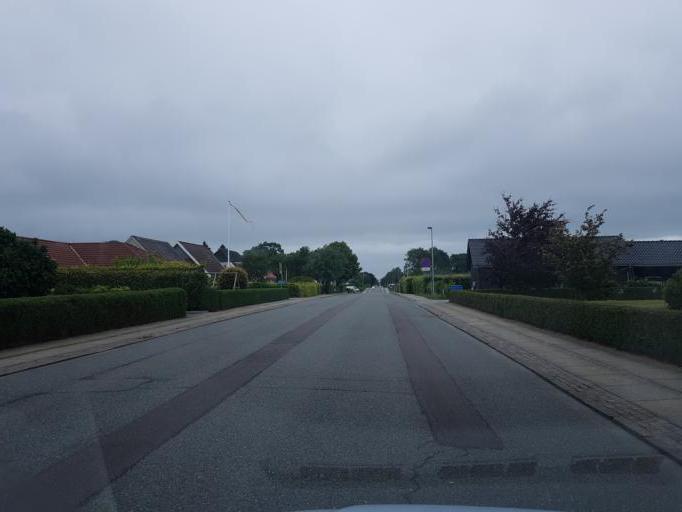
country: DK
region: South Denmark
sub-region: Varde Kommune
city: Varde
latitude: 55.6111
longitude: 8.4722
